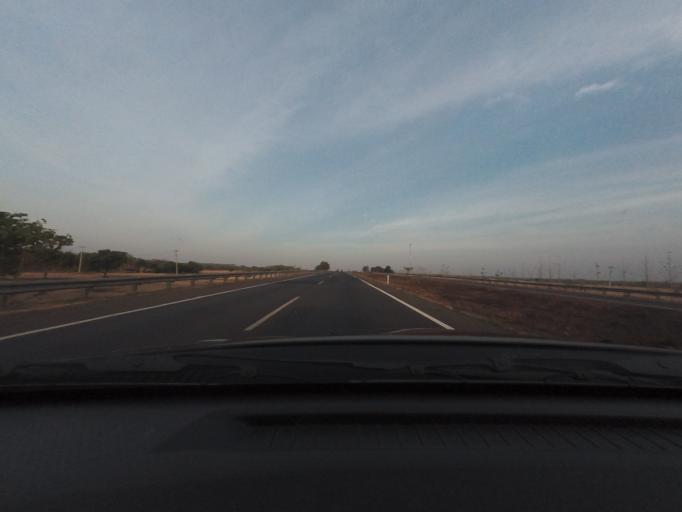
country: ID
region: West Java
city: Pamanukan
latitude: -6.5372
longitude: 107.8493
